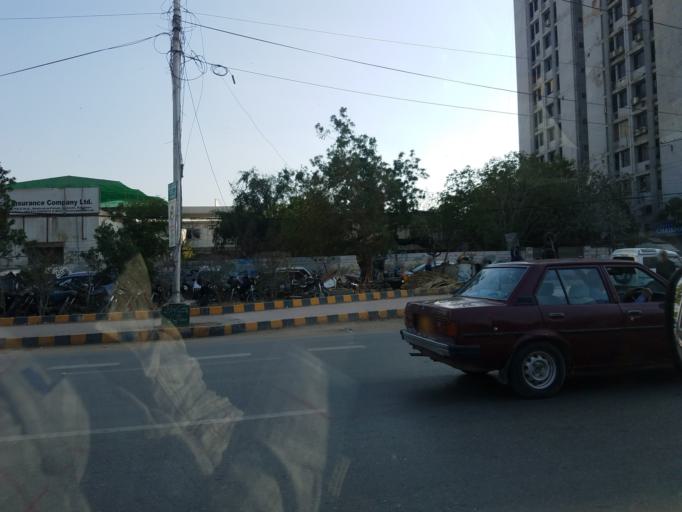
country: PK
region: Sindh
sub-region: Karachi District
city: Karachi
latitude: 24.8625
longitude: 67.0711
